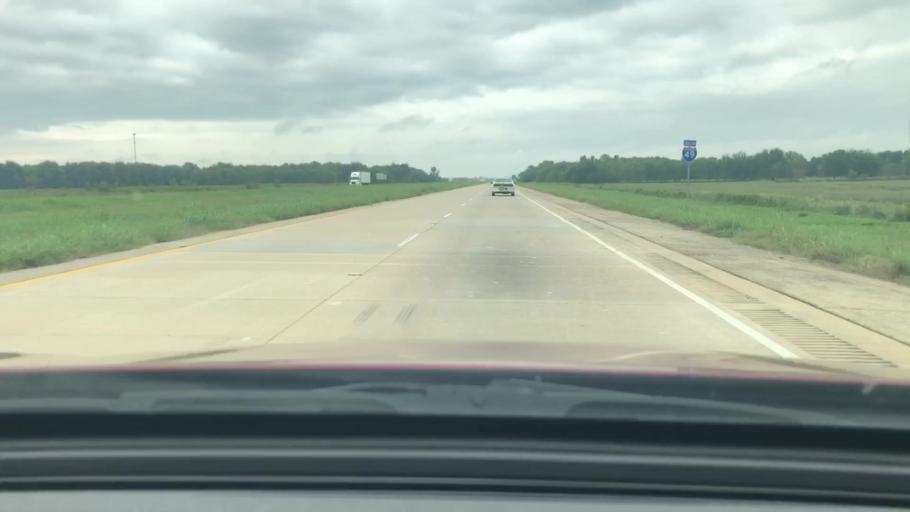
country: US
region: Louisiana
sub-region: Bossier Parish
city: Benton
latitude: 32.6934
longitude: -93.8580
